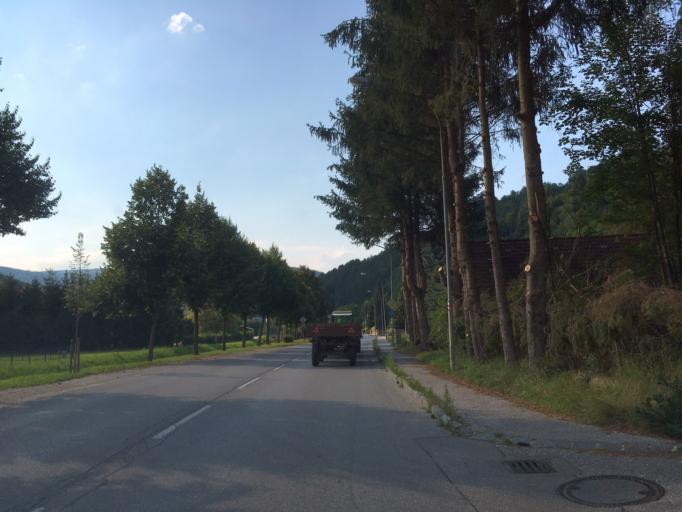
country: AT
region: Lower Austria
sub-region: Politischer Bezirk Neunkirchen
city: Grimmenstein
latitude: 47.6003
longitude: 16.1372
